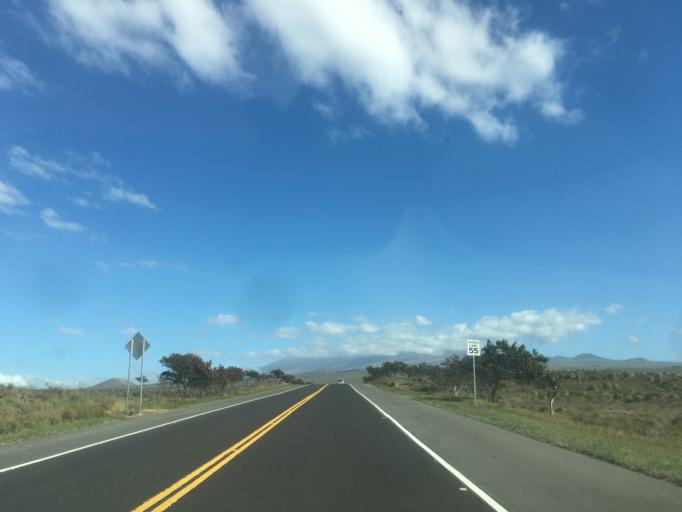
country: US
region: Hawaii
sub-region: Hawaii County
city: Waikoloa
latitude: 19.9066
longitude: -155.7672
